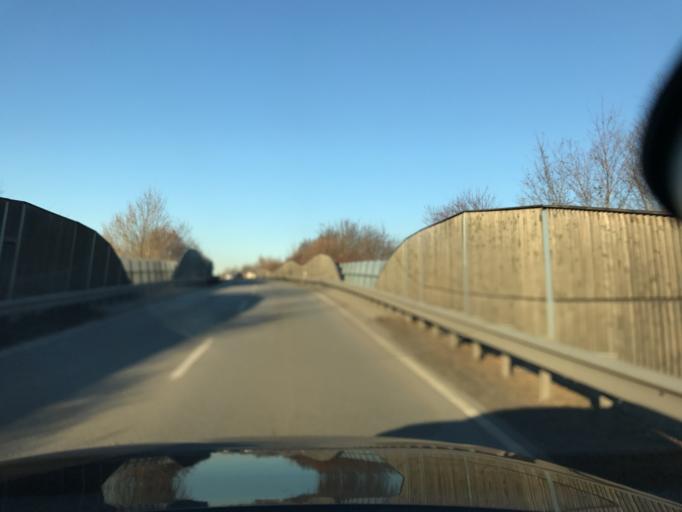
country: DE
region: Bavaria
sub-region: Upper Bavaria
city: Bad Aibling
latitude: 47.8646
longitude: 11.9881
